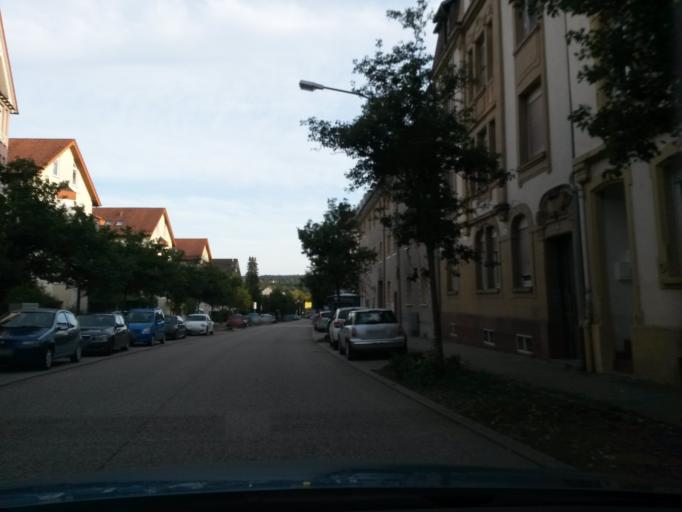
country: DE
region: Baden-Wuerttemberg
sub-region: Karlsruhe Region
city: Ispringen
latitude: 48.8921
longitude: 8.6632
